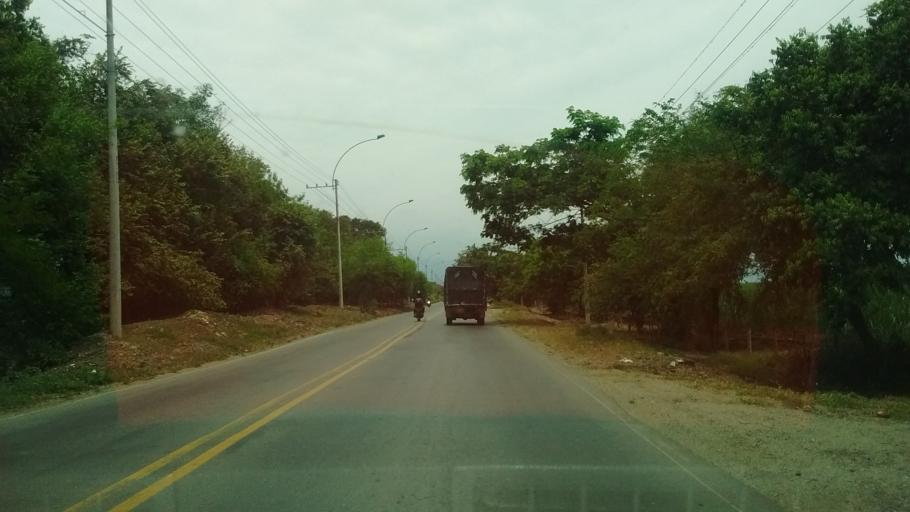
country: CO
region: Valle del Cauca
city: Jamundi
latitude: 3.3225
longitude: -76.4984
